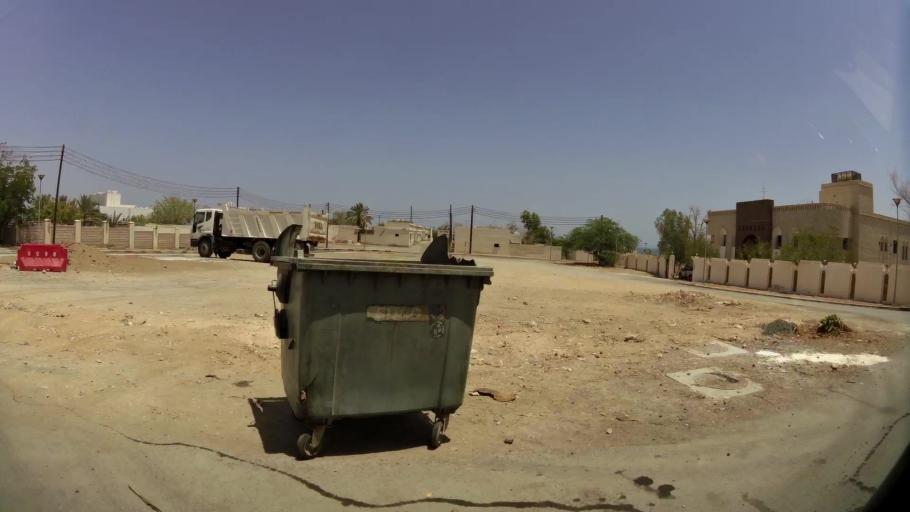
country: OM
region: Muhafazat Masqat
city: Bawshar
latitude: 23.6080
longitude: 58.4680
